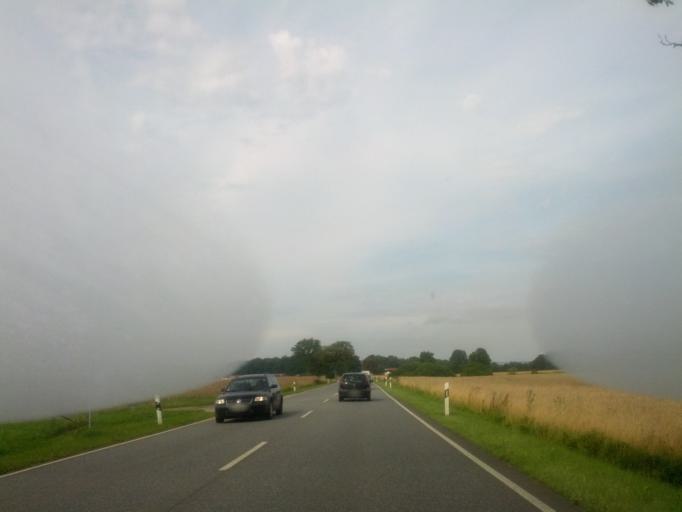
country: DE
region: Mecklenburg-Vorpommern
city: Neubukow
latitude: 54.0191
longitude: 11.6560
